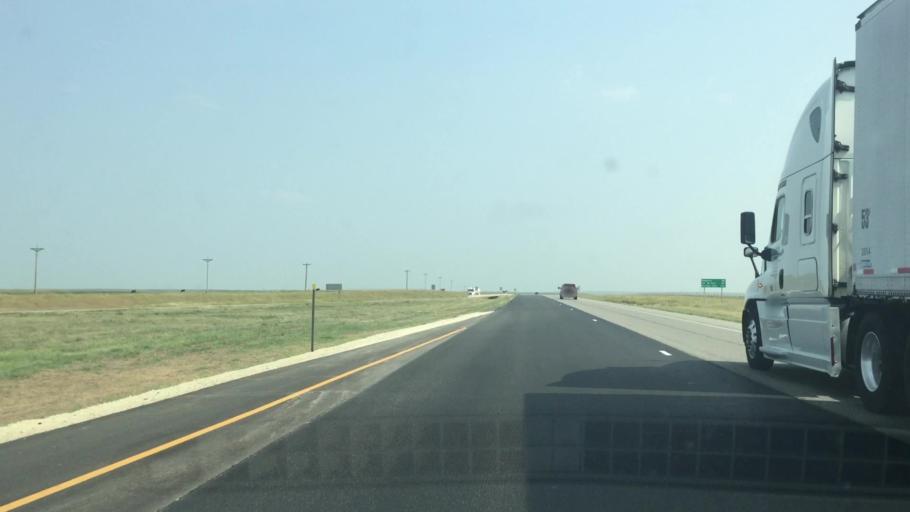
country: US
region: Kansas
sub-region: Chase County
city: Cottonwood Falls
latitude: 38.1008
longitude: -96.5762
